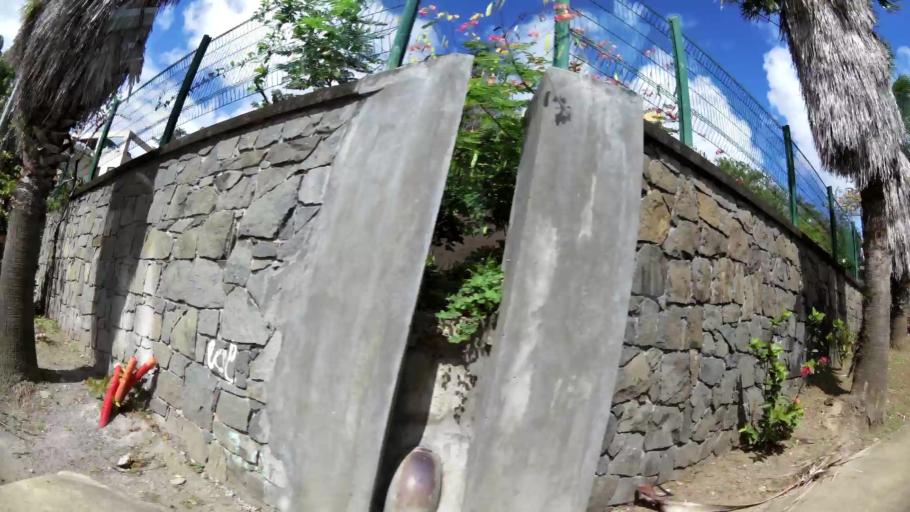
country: MQ
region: Martinique
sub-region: Martinique
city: Fort-de-France
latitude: 14.6031
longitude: -61.0630
